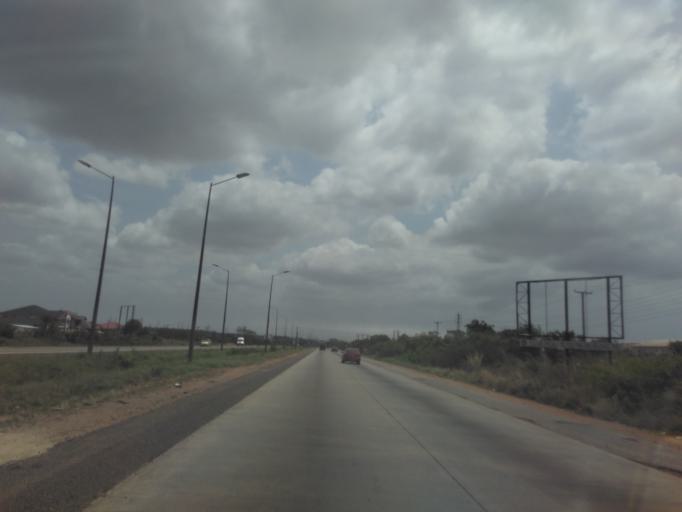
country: GH
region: Greater Accra
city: Nungua
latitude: 5.6536
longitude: -0.0967
